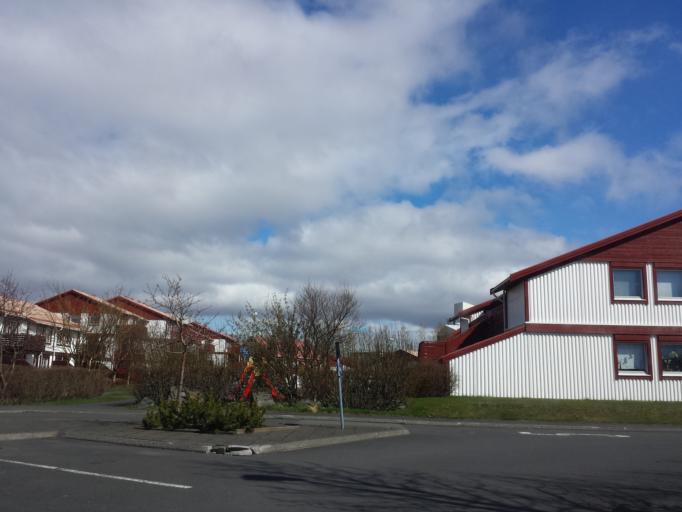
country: IS
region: Capital Region
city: Kopavogur
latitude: 64.1057
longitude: -21.8845
